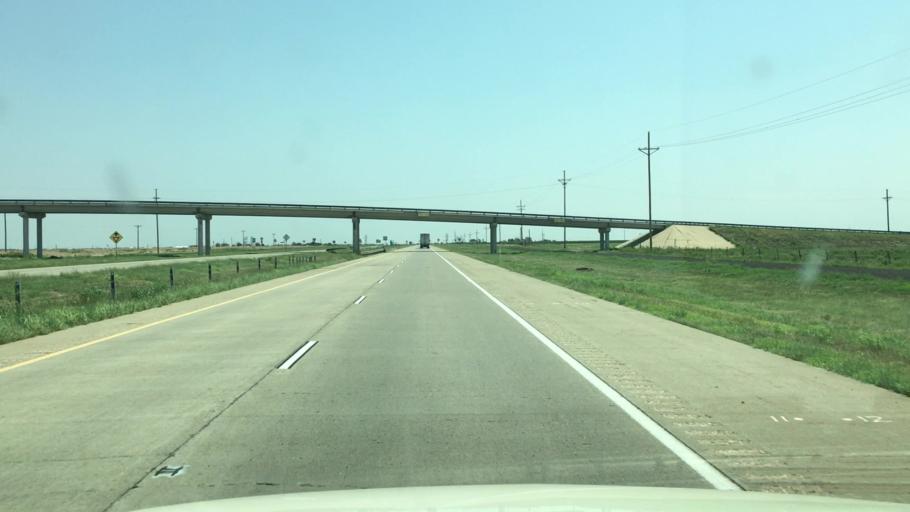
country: US
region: Texas
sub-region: Potter County
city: Bushland
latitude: 35.1962
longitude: -102.1161
